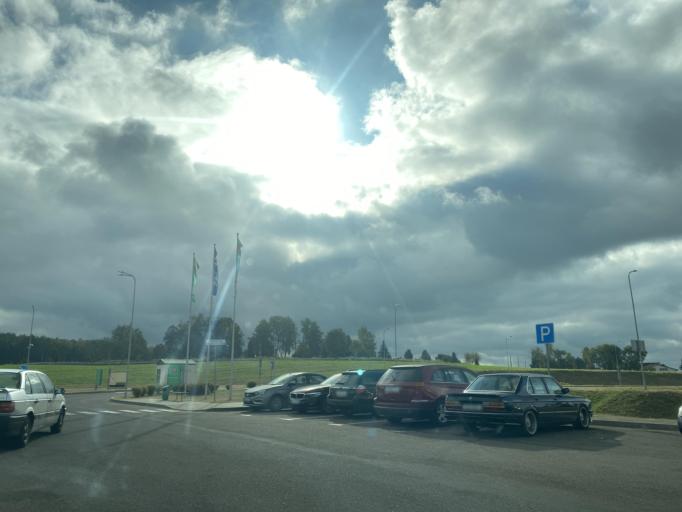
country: BY
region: Minsk
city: Bal'shavik
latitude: 53.9794
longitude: 27.5367
